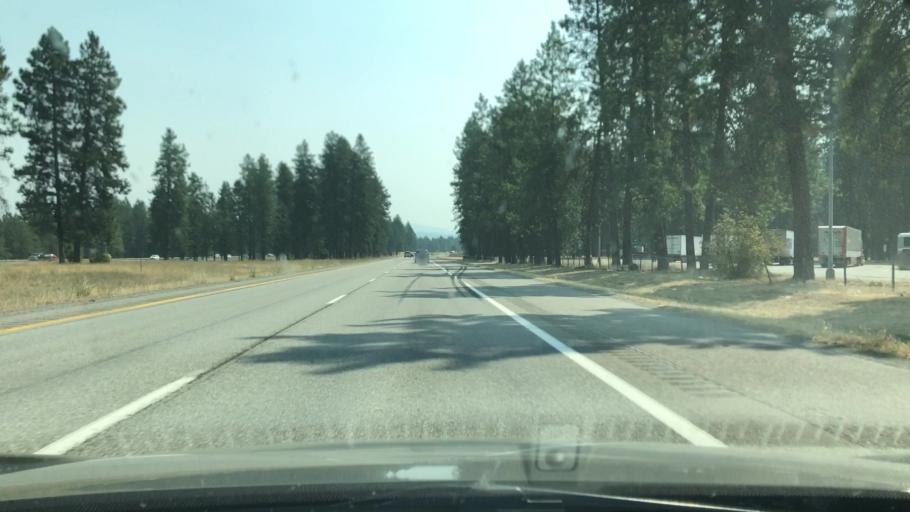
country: US
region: Idaho
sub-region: Kootenai County
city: Post Falls
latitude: 47.7085
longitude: -116.8662
